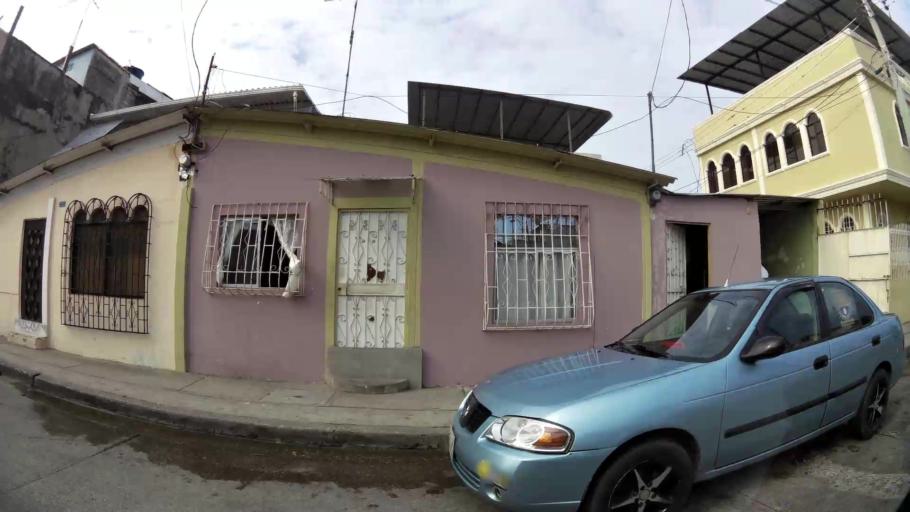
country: EC
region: Guayas
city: Guayaquil
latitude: -2.2473
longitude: -79.8873
